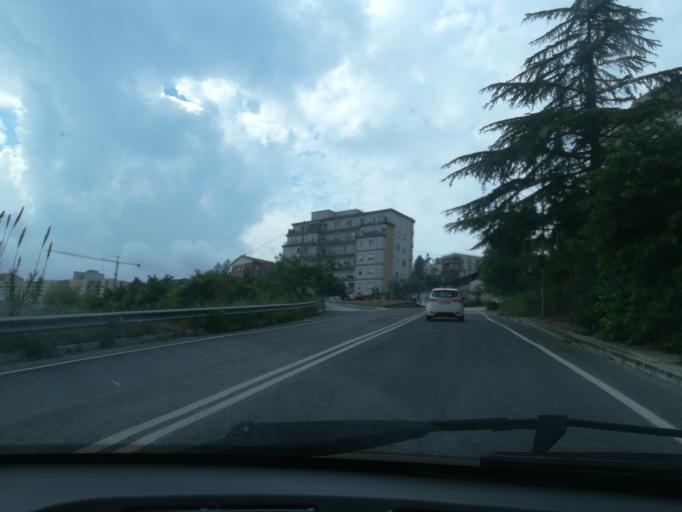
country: IT
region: The Marches
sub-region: Provincia di Macerata
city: Macerata
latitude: 43.3052
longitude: 13.4395
